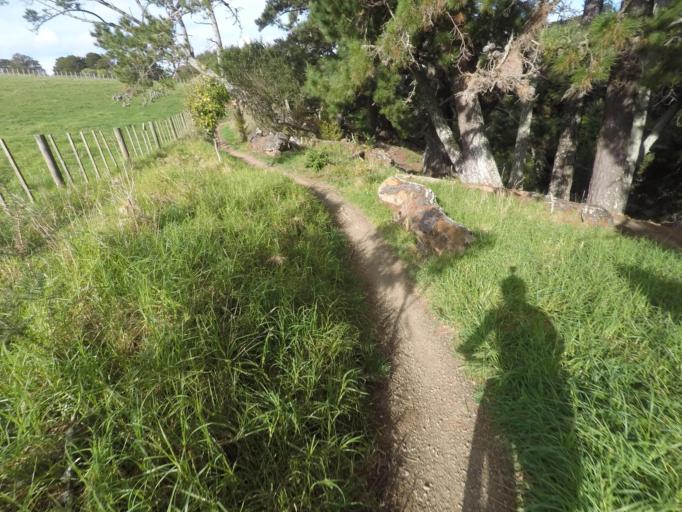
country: NZ
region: Auckland
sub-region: Auckland
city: Manukau City
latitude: -36.9943
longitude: 174.9109
